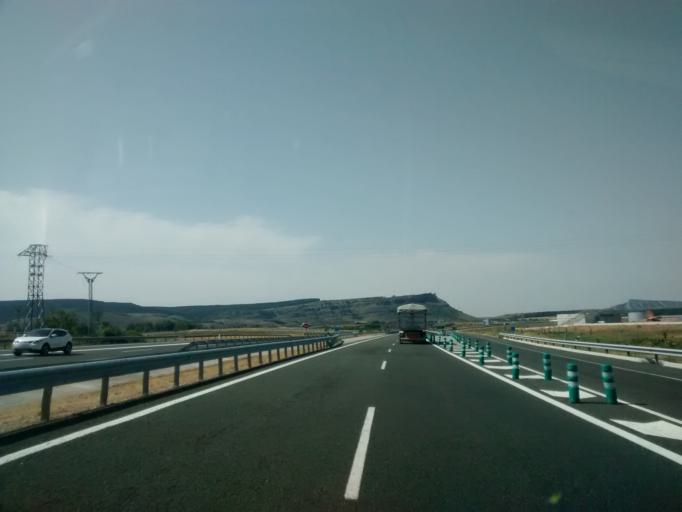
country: ES
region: Castille and Leon
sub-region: Provincia de Palencia
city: Aguilar de Campoo
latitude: 42.7854
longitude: -4.2381
